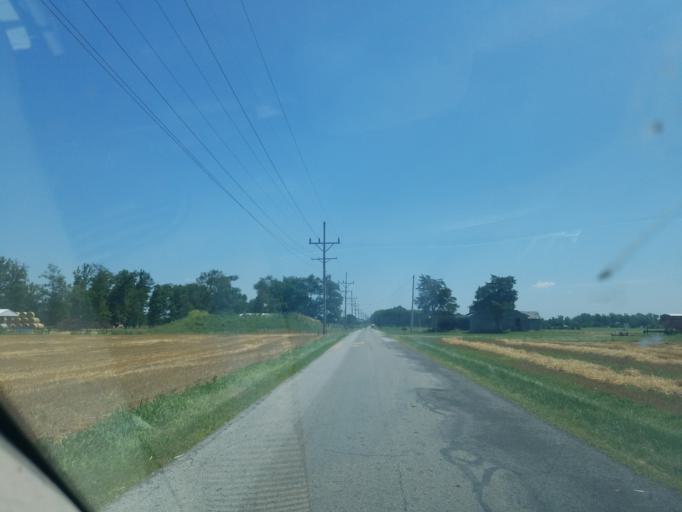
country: US
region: Ohio
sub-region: Allen County
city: Delphos
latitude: 40.7794
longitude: -84.3225
